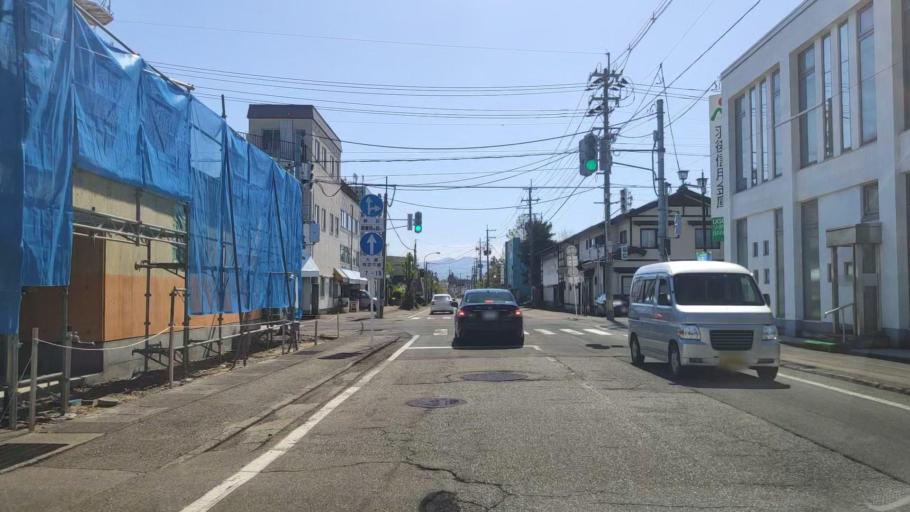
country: JP
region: Akita
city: Omagari
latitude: 39.4586
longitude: 140.4776
